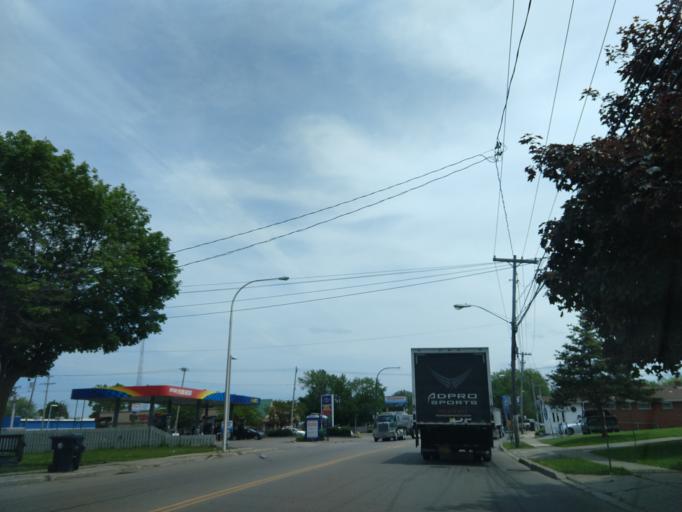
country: US
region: New York
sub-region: Erie County
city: Lackawanna
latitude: 42.8282
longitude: -78.8056
